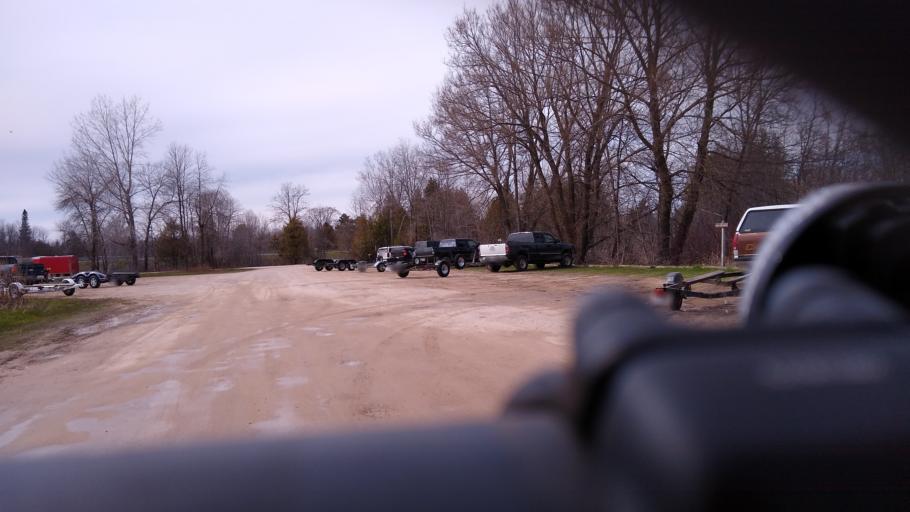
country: US
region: Michigan
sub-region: Delta County
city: Escanaba
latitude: 45.6770
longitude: -87.1411
